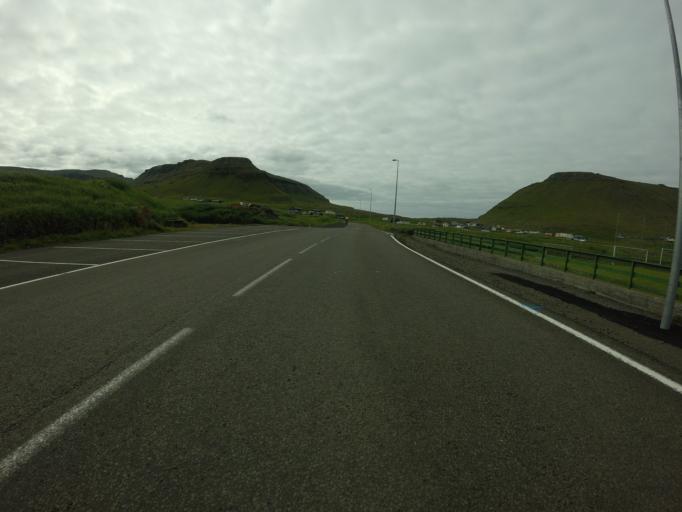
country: FO
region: Suduroy
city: Tvoroyri
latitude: 61.6018
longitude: -6.9520
